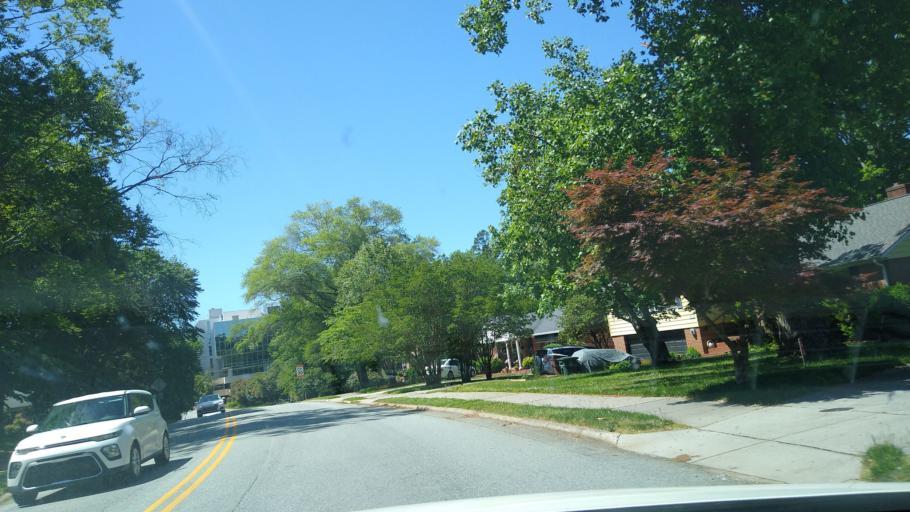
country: US
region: North Carolina
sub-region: Guilford County
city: Greensboro
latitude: 36.0909
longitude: -79.8327
